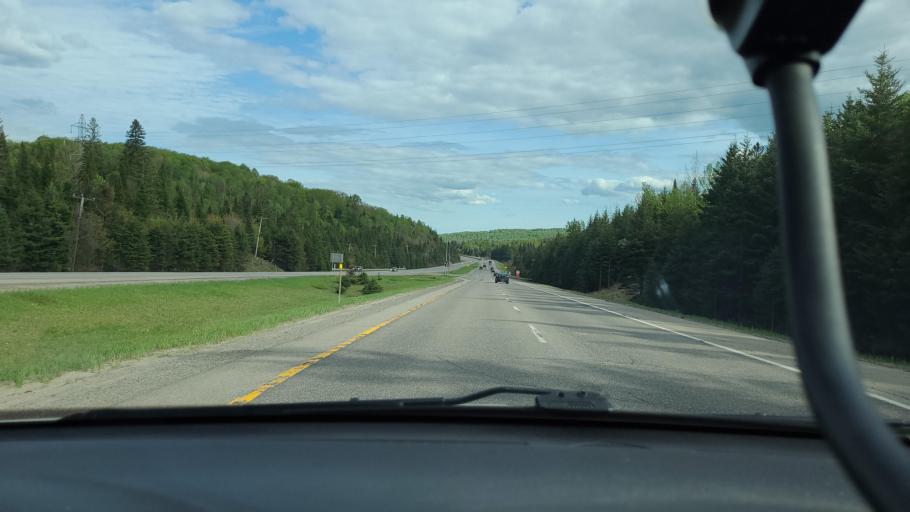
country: CA
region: Quebec
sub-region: Laurentides
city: Sainte-Agathe-des-Monts
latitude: 46.0853
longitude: -74.3237
